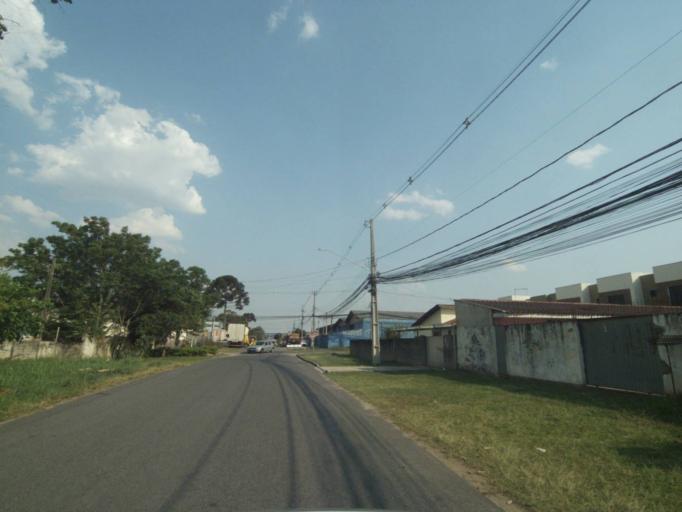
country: BR
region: Parana
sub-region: Sao Jose Dos Pinhais
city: Sao Jose dos Pinhais
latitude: -25.5339
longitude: -49.2357
